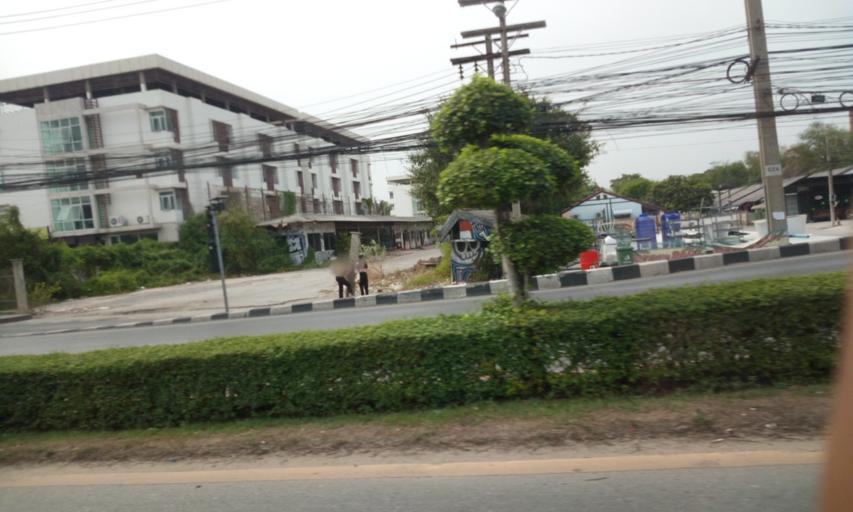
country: TH
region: Bangkok
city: Lat Krabang
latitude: 13.7218
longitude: 100.7783
